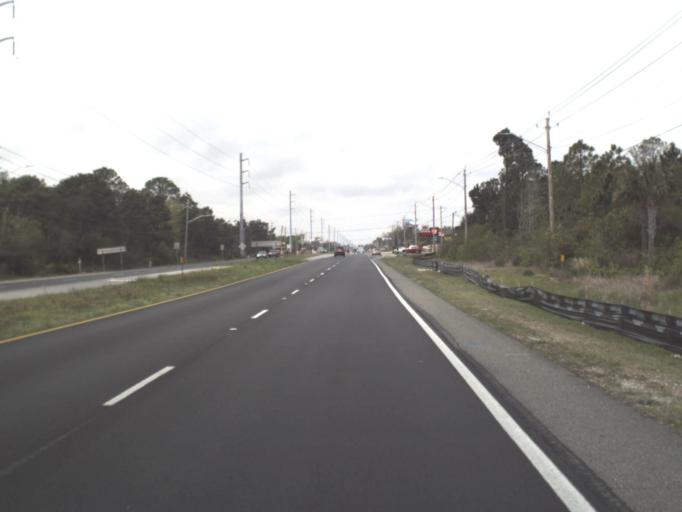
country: US
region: Florida
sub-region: Santa Rosa County
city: Woodlawn Beach
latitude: 30.4003
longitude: -86.9971
